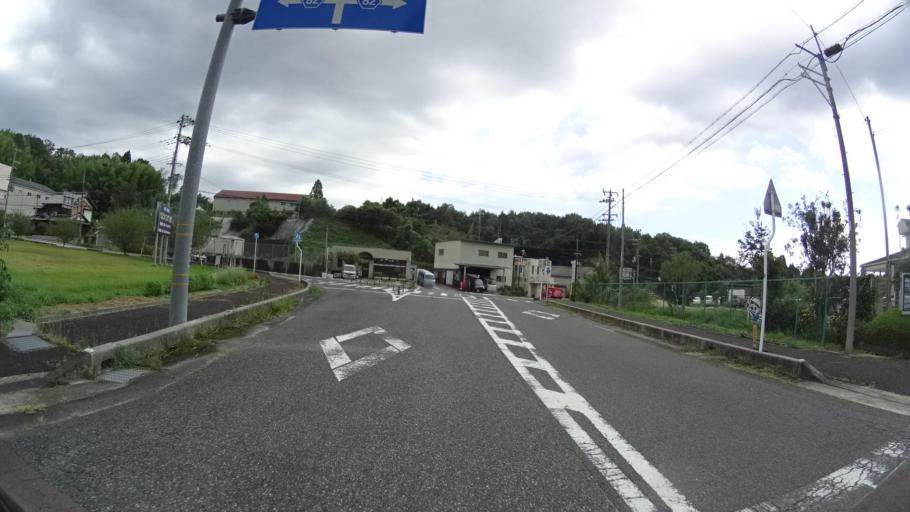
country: JP
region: Mie
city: Ueno-ebisumachi
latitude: 34.7117
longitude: 136.0452
